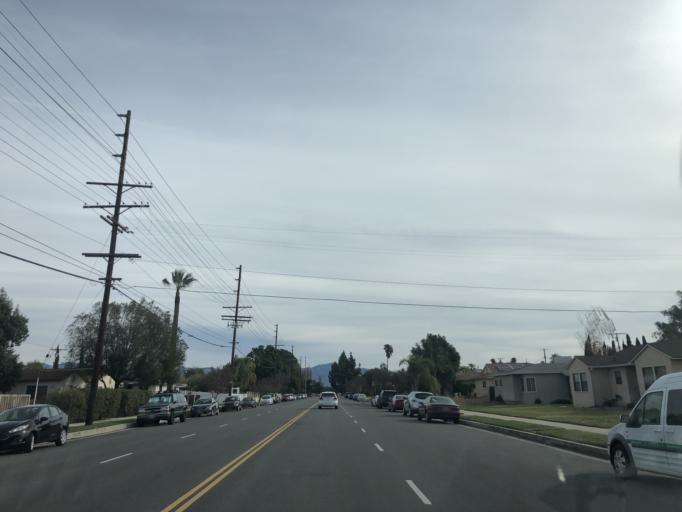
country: US
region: California
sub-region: Los Angeles County
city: San Fernando
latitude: 34.2720
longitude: -118.4834
